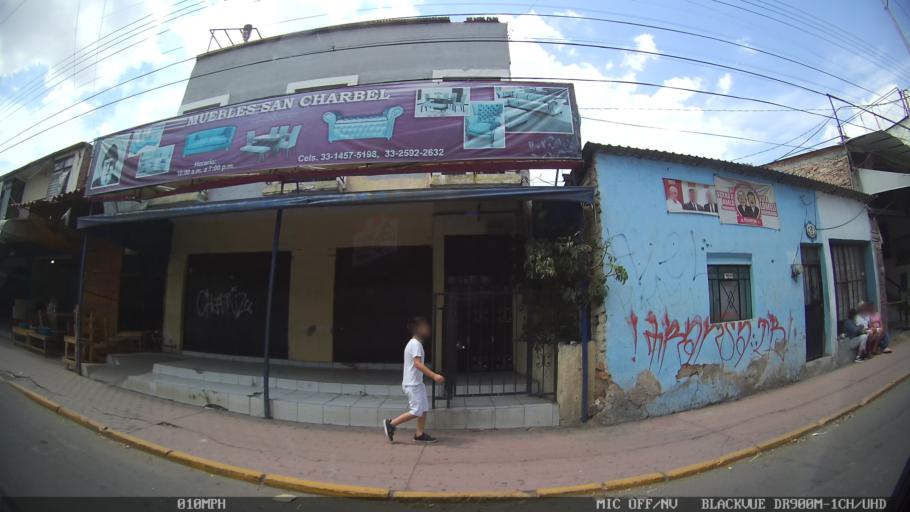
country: MX
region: Jalisco
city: Tonala
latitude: 20.6253
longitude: -103.2480
